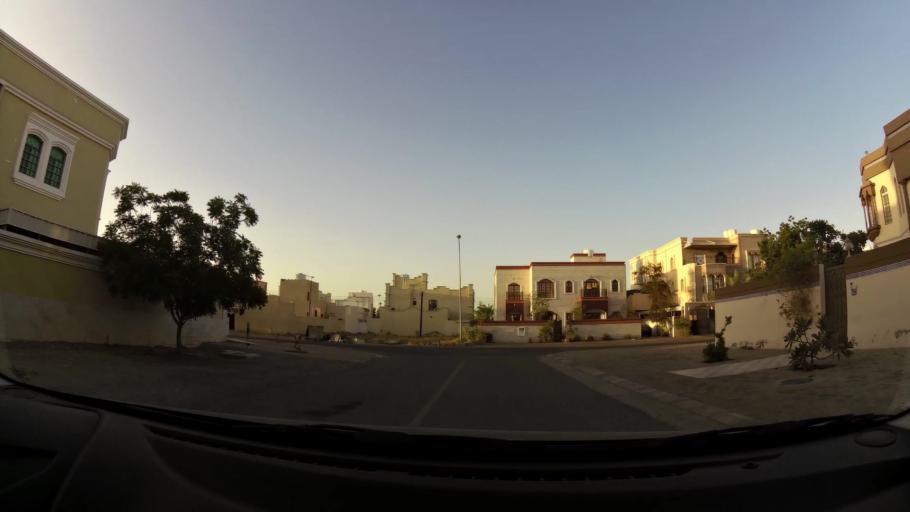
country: OM
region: Muhafazat Masqat
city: As Sib al Jadidah
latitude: 23.6030
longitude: 58.2312
